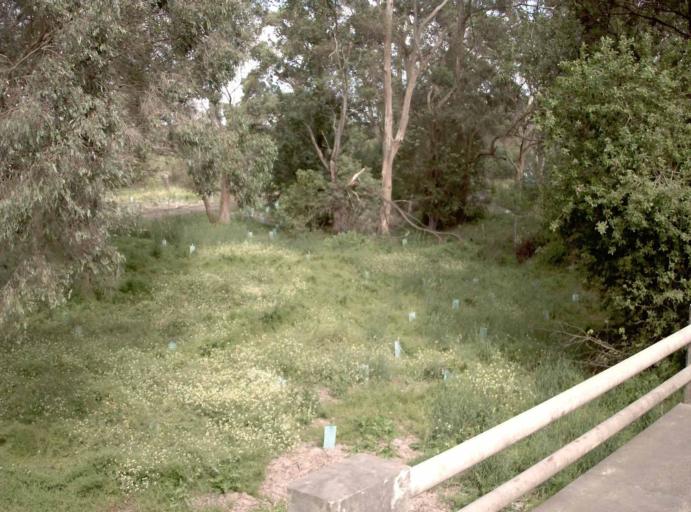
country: AU
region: Victoria
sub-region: Latrobe
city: Morwell
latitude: -38.1669
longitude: 146.4107
